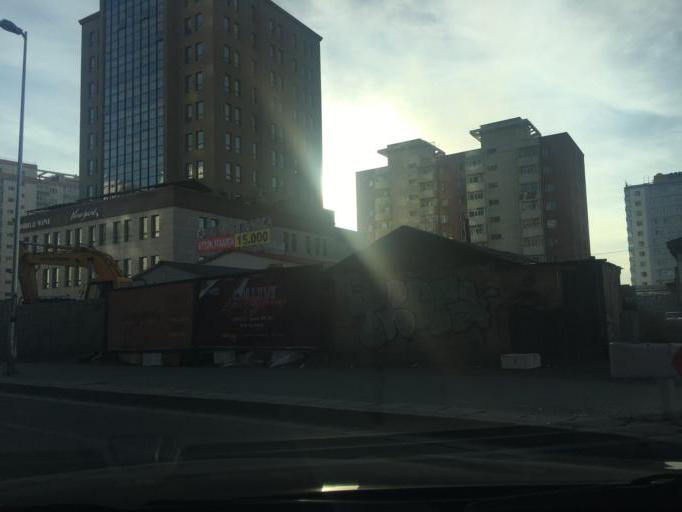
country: MN
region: Ulaanbaatar
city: Ulaanbaatar
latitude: 47.9072
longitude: 106.8948
